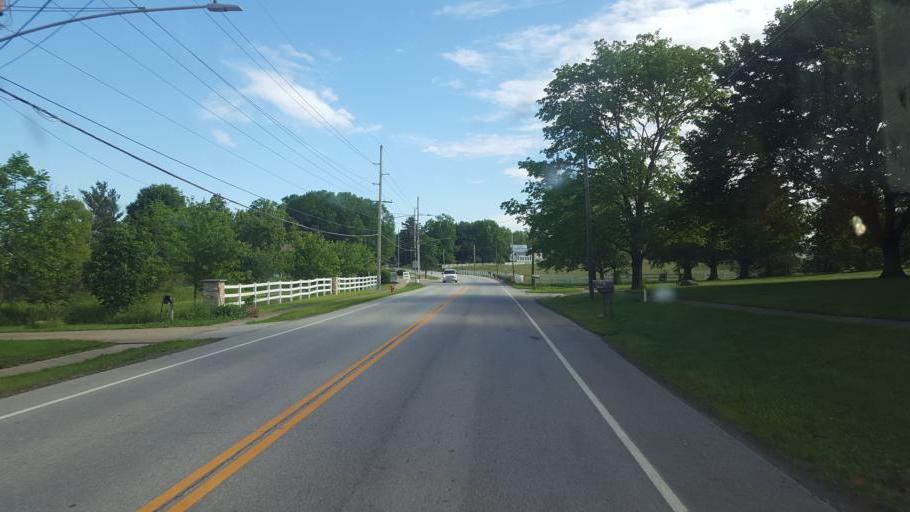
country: US
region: Ohio
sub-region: Medina County
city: Seville
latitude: 41.0191
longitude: -81.8618
